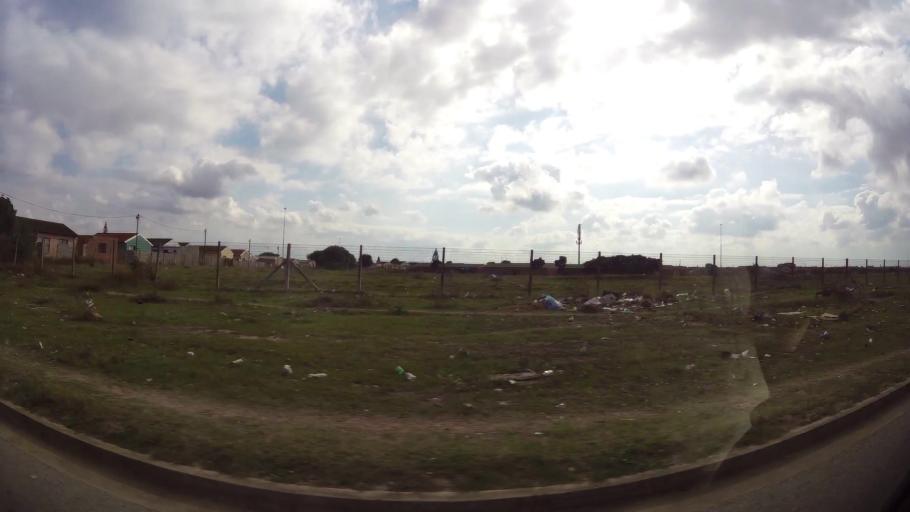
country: ZA
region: Eastern Cape
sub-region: Nelson Mandela Bay Metropolitan Municipality
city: Port Elizabeth
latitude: -33.8192
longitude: 25.5937
